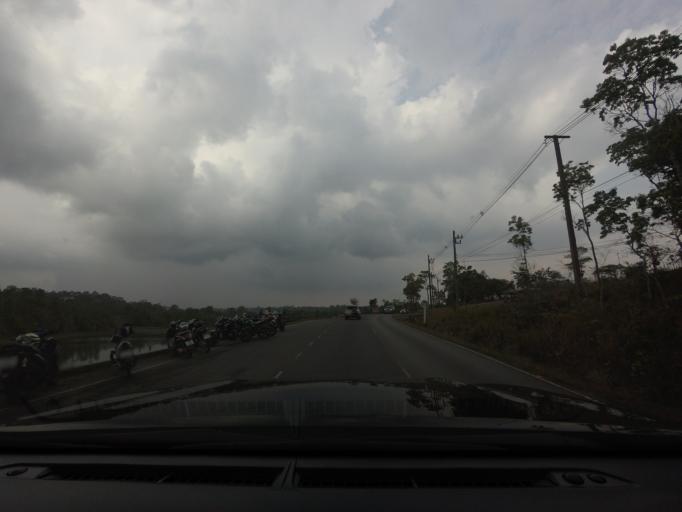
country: TH
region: Nakhon Nayok
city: Nakhon Nayok
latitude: 14.4312
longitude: 101.3699
